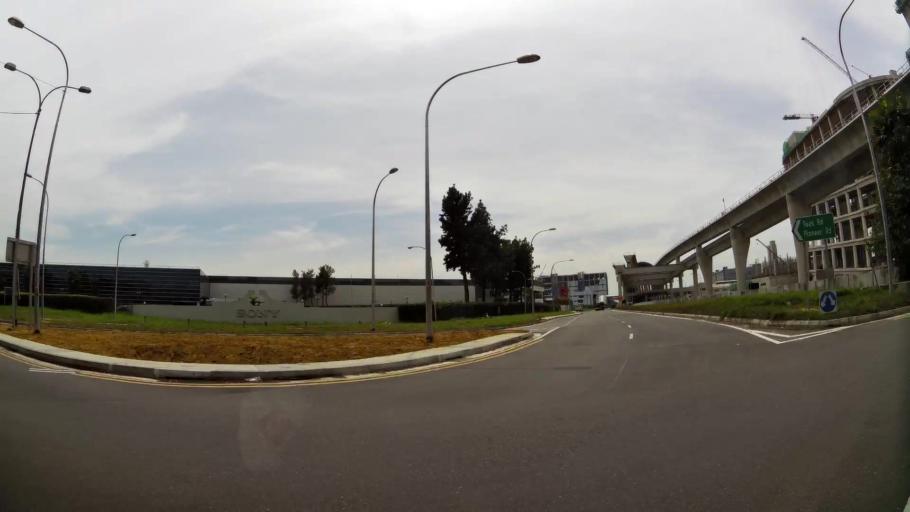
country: MY
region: Johor
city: Johor Bahru
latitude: 1.3224
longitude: 103.6635
